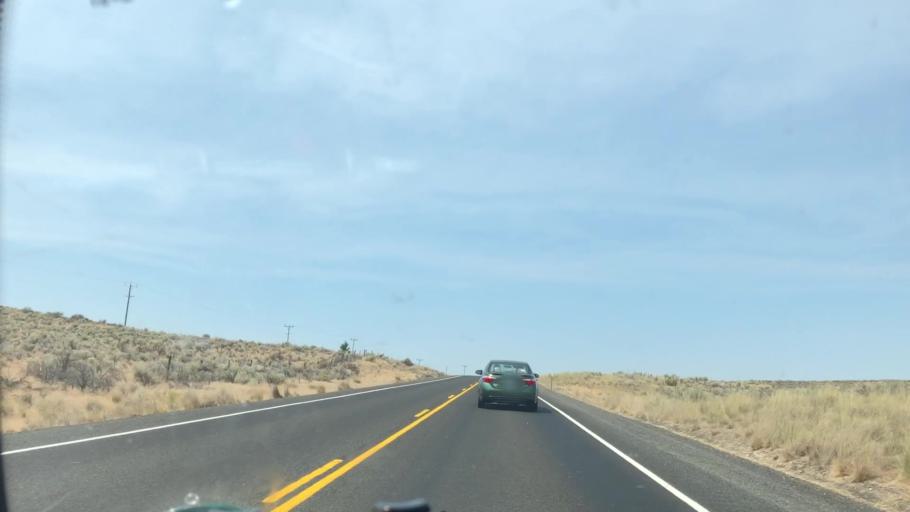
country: US
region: Idaho
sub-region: Owyhee County
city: Murphy
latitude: 42.9917
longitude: -117.0586
